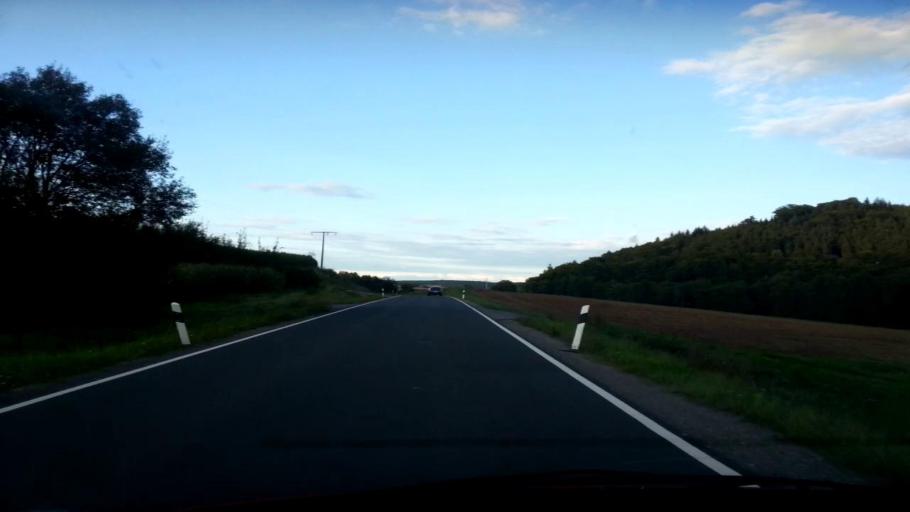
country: DE
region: Bavaria
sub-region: Upper Franconia
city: Burgwindheim
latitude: 49.8202
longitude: 10.5585
